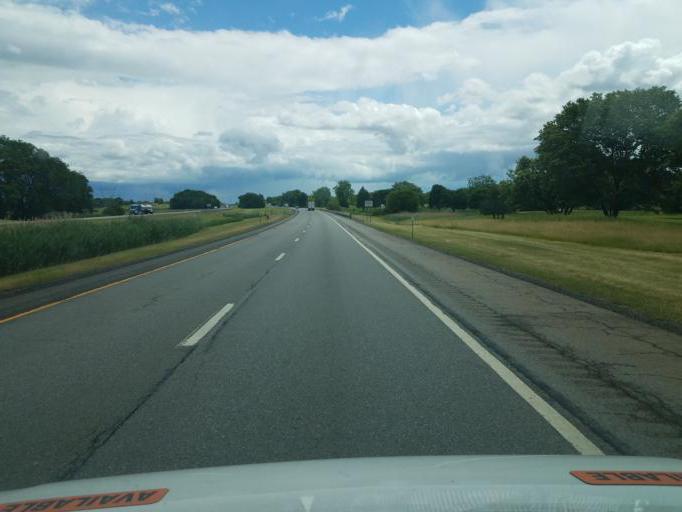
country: US
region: New York
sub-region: Monroe County
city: Honeoye Falls
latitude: 43.0470
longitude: -77.6182
